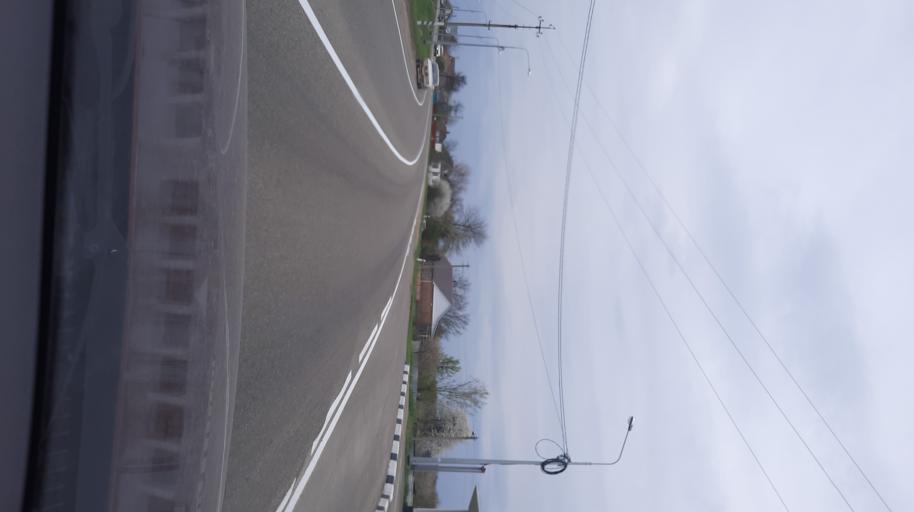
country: RU
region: Krasnodarskiy
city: Dneprovskaya
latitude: 45.6756
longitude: 38.8475
